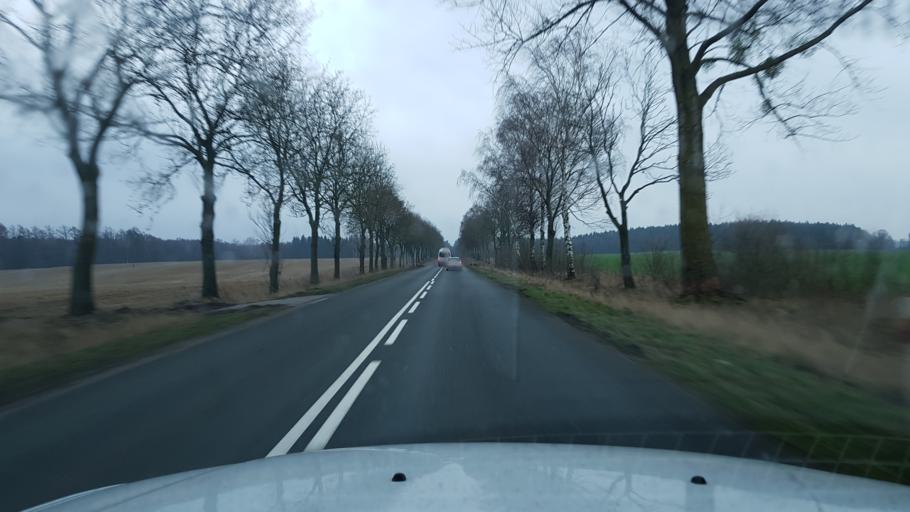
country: PL
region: West Pomeranian Voivodeship
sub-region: Powiat gryficki
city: Gryfice
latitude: 53.8667
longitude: 15.2184
